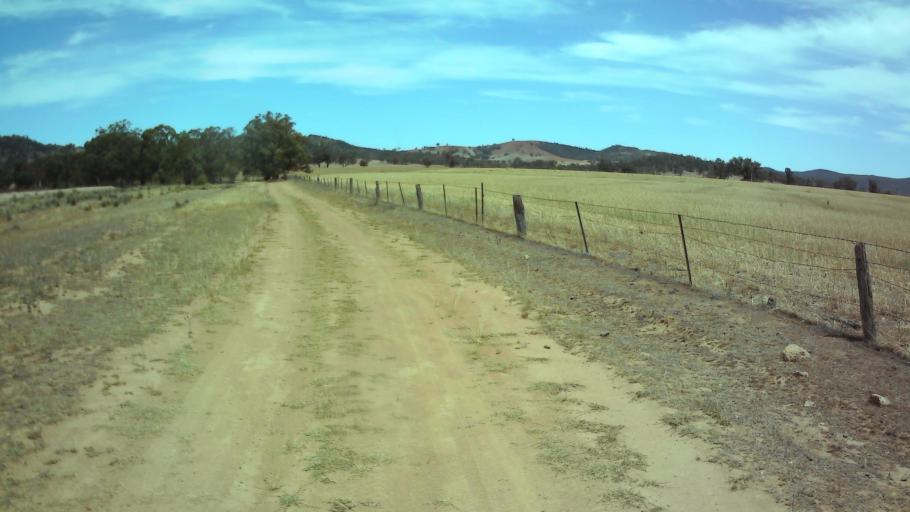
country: AU
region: New South Wales
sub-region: Weddin
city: Grenfell
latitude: -33.7617
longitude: 148.1455
